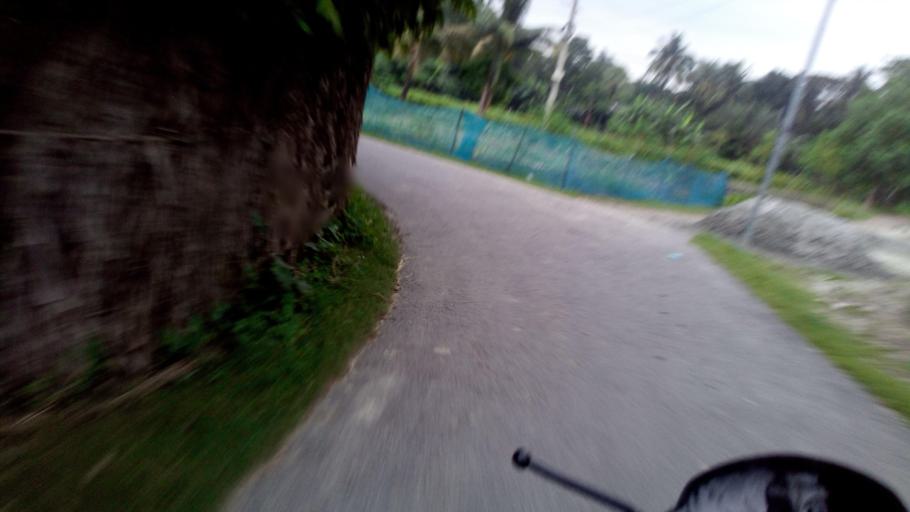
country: BD
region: Khulna
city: Phultala
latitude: 22.7678
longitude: 89.4079
